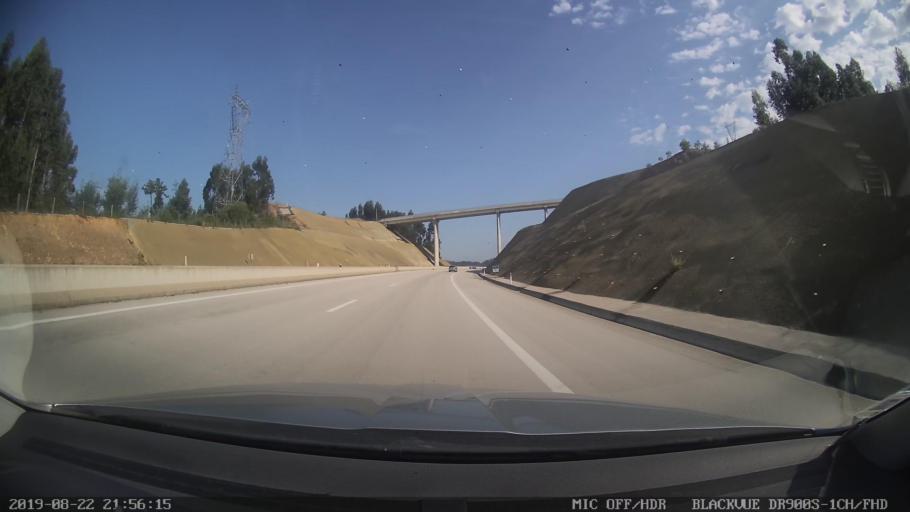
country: PT
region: Coimbra
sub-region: Coimbra
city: Coimbra
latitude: 40.1669
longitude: -8.3783
